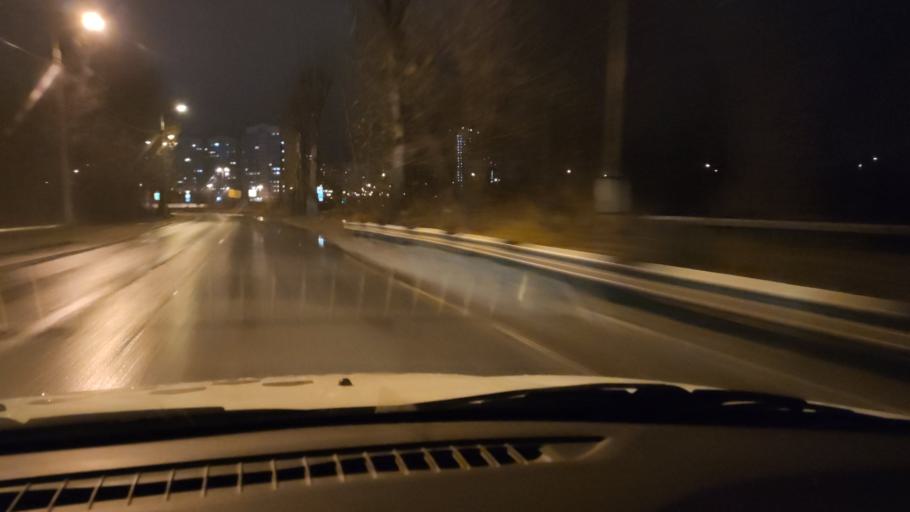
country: RU
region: Perm
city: Kondratovo
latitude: 58.0023
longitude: 56.1298
